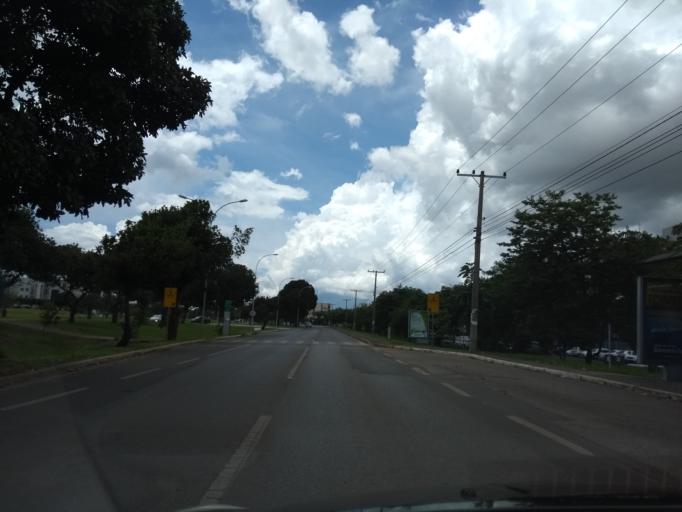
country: BR
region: Federal District
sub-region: Brasilia
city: Brasilia
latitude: -15.7905
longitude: -47.9329
